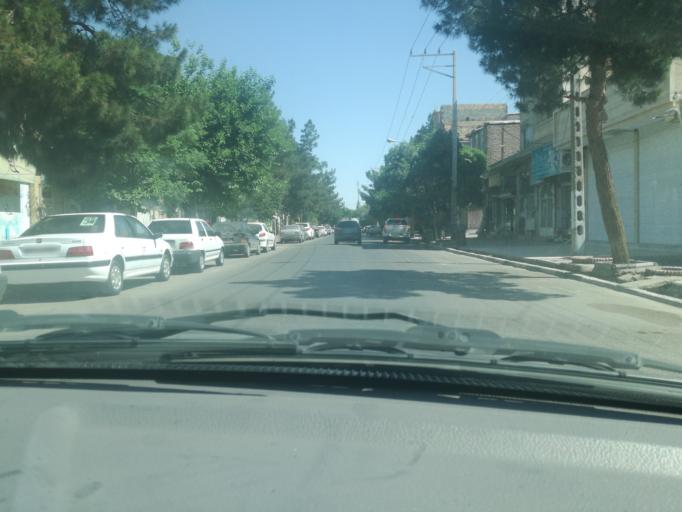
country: IR
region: Razavi Khorasan
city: Sarakhs
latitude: 36.5401
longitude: 61.1637
